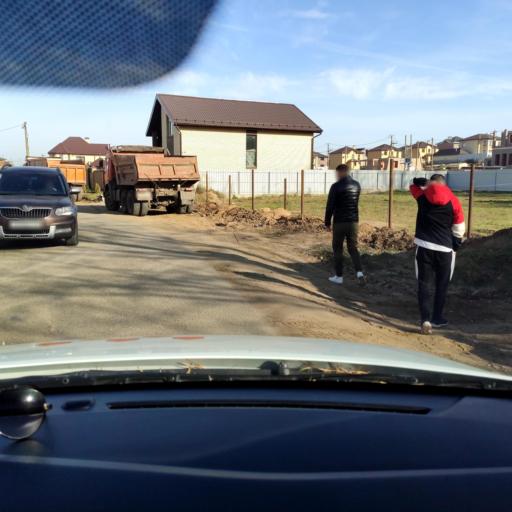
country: RU
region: Tatarstan
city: Vysokaya Gora
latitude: 55.7867
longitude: 49.2610
